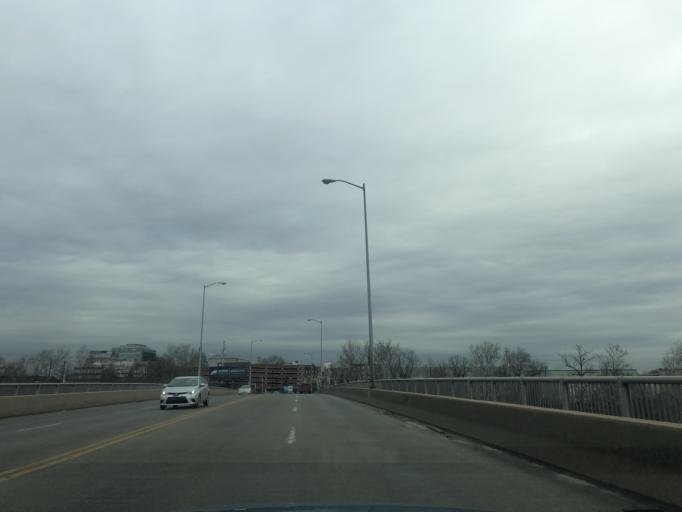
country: US
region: Pennsylvania
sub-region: Montgomery County
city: Bridgeport
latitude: 40.1093
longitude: -75.3447
